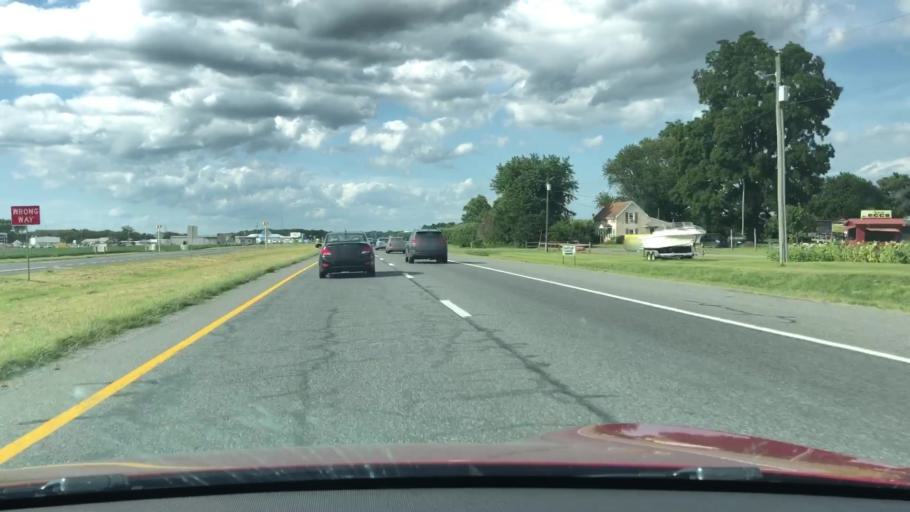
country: US
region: Delaware
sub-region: Sussex County
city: Bridgeville
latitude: 38.7496
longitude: -75.5931
